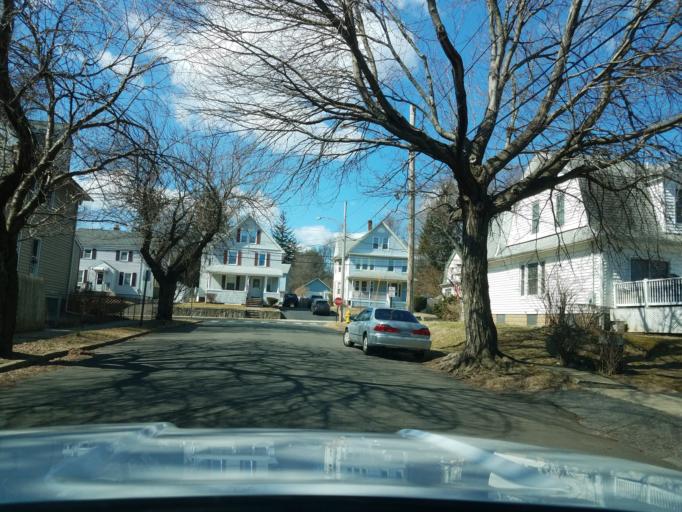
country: US
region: Connecticut
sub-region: Fairfield County
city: Stratford
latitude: 41.1944
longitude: -73.1364
